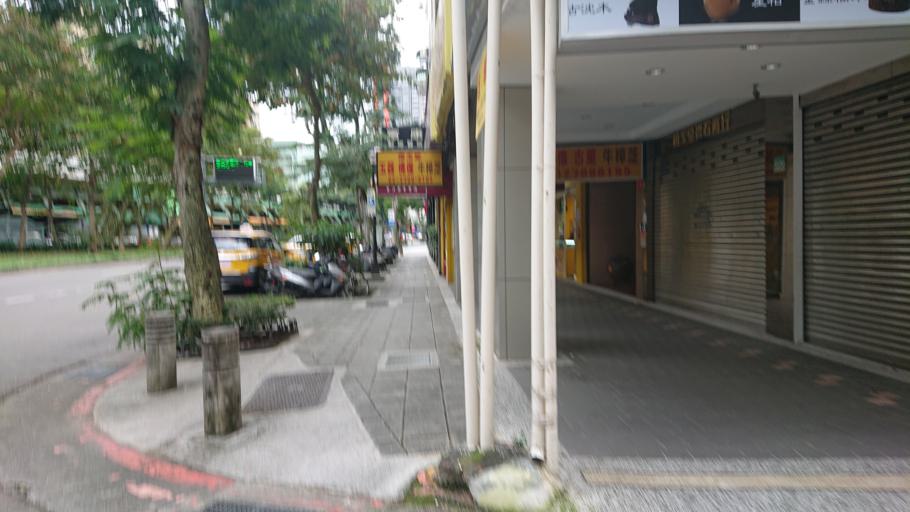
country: TW
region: Taipei
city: Taipei
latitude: 25.0362
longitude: 121.5374
